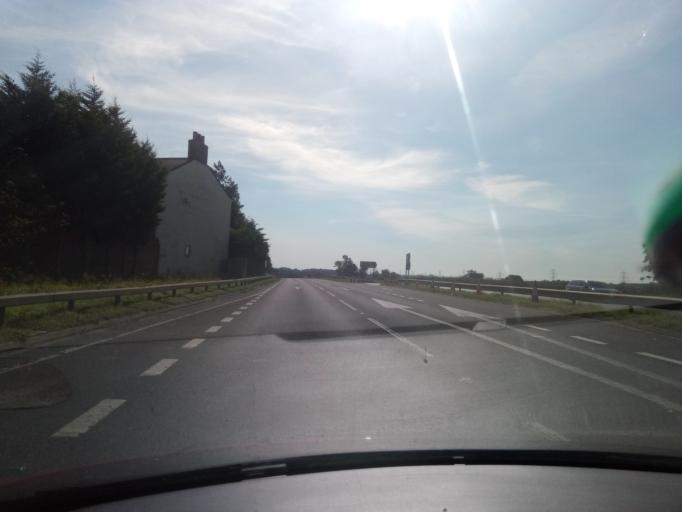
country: GB
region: England
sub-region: Stockton-on-Tees
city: Yarm
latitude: 54.3928
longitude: -1.3195
